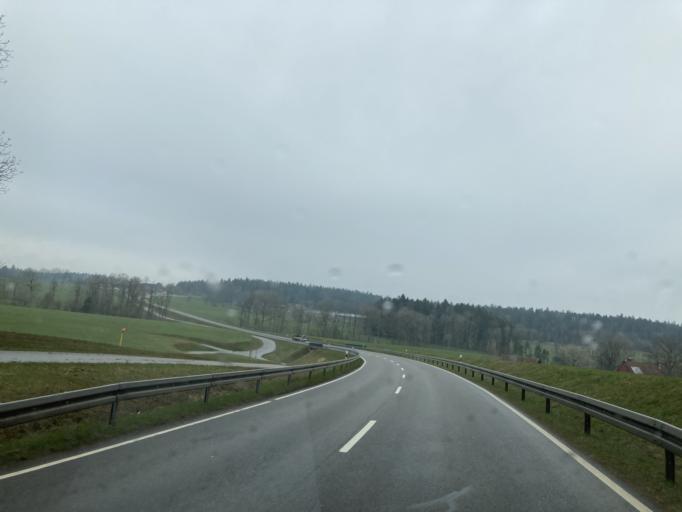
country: DE
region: Baden-Wuerttemberg
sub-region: Karlsruhe Region
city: Lossburg
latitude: 48.3662
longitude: 8.4477
